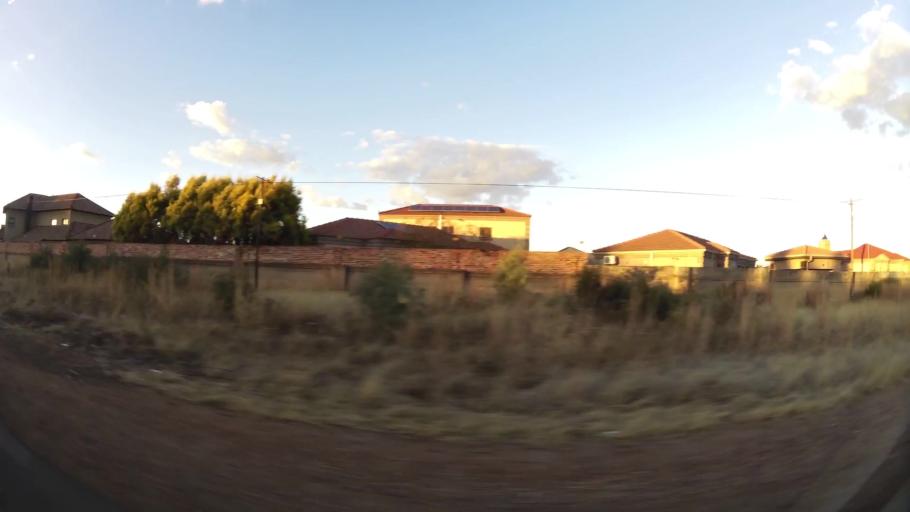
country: ZA
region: North-West
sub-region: Dr Kenneth Kaunda District Municipality
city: Potchefstroom
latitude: -26.7250
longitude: 27.1164
